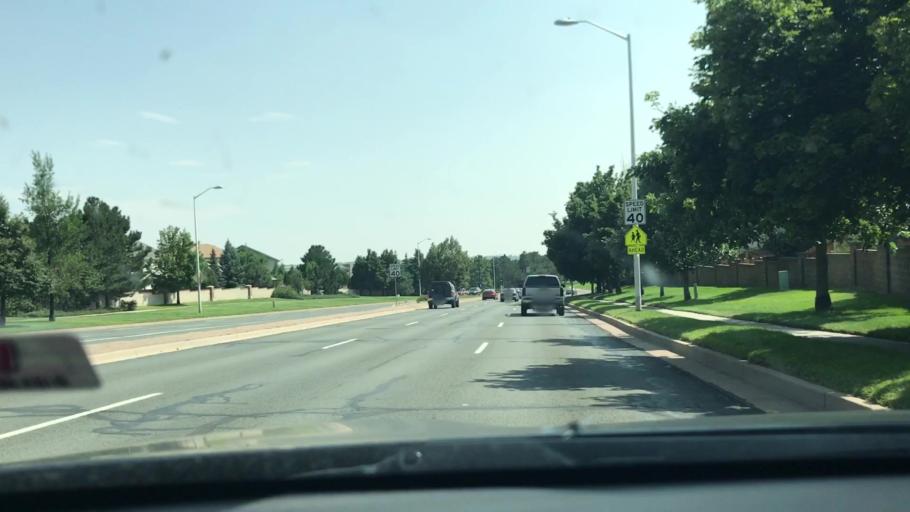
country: US
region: Colorado
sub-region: El Paso County
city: Black Forest
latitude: 38.9548
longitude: -104.7645
